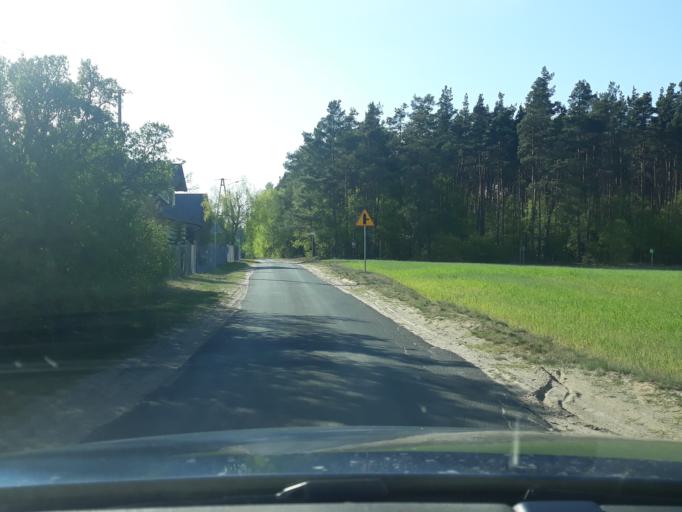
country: PL
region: Pomeranian Voivodeship
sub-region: Powiat czluchowski
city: Przechlewo
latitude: 53.8813
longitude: 17.3222
